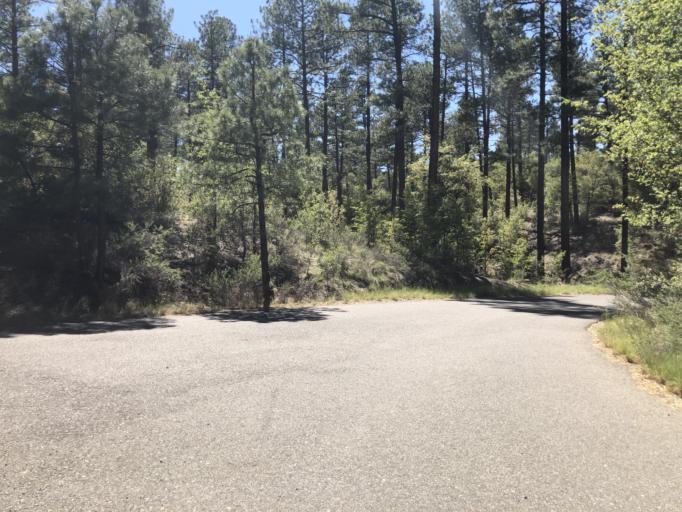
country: US
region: Arizona
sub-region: Yavapai County
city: Prescott
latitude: 34.5145
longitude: -112.3884
